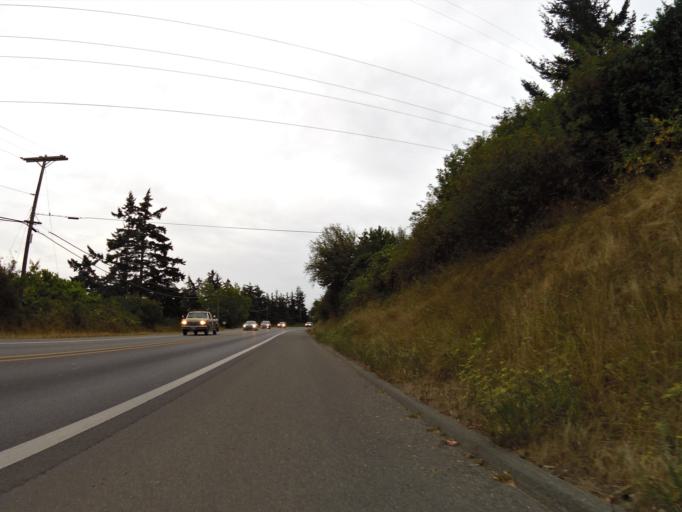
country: US
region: Washington
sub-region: Jefferson County
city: Port Townsend
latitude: 48.1052
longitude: -122.7853
